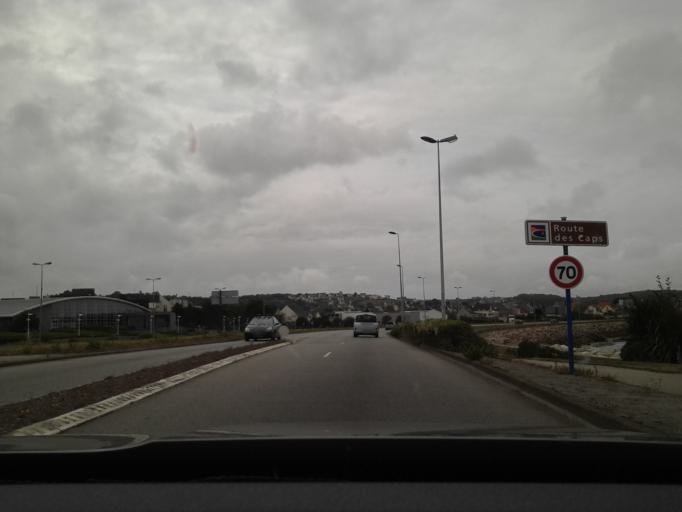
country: FR
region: Lower Normandy
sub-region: Departement de la Manche
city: Equeurdreville-Hainneville
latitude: 49.6577
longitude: -1.6688
